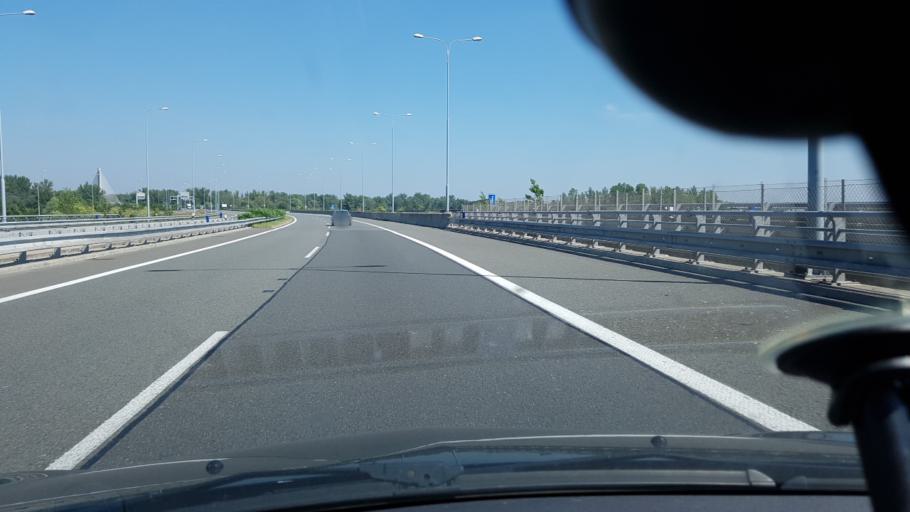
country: PL
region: Silesian Voivodeship
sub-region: Powiat raciborski
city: Chalupki
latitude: 49.8801
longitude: 18.3052
